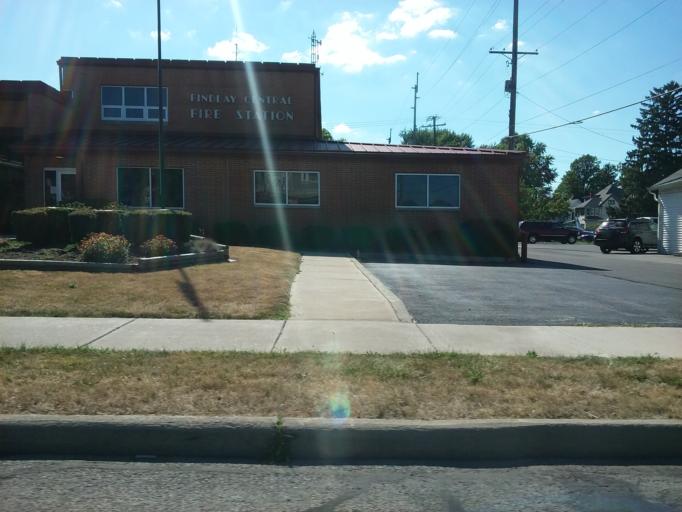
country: US
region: Ohio
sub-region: Hancock County
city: Findlay
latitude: 41.0337
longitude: -83.6503
